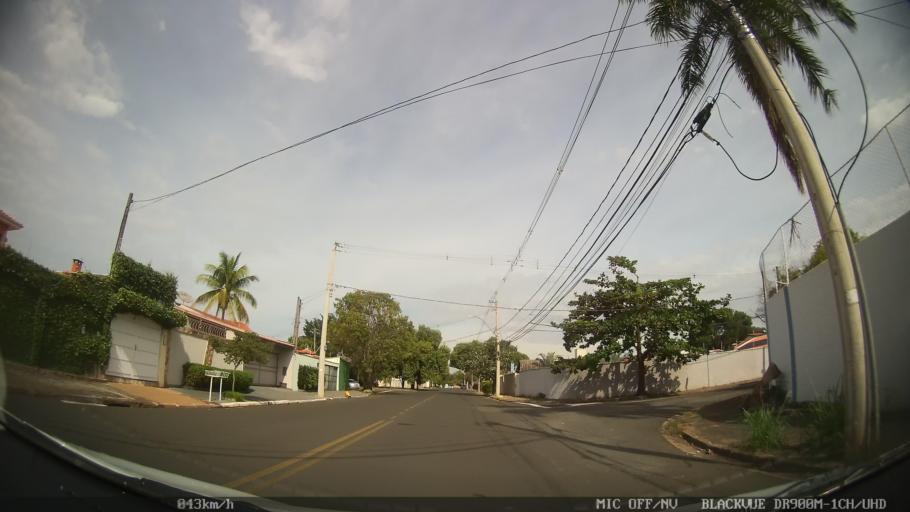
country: BR
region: Sao Paulo
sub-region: Piracicaba
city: Piracicaba
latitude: -22.7084
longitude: -47.6725
